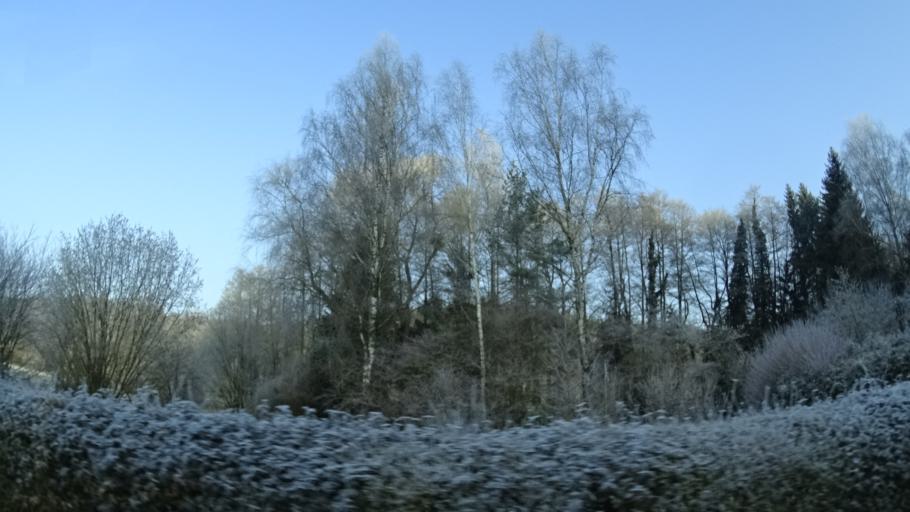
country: DE
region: Bavaria
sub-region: Upper Franconia
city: Weitramsdorf
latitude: 50.2427
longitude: 10.8947
